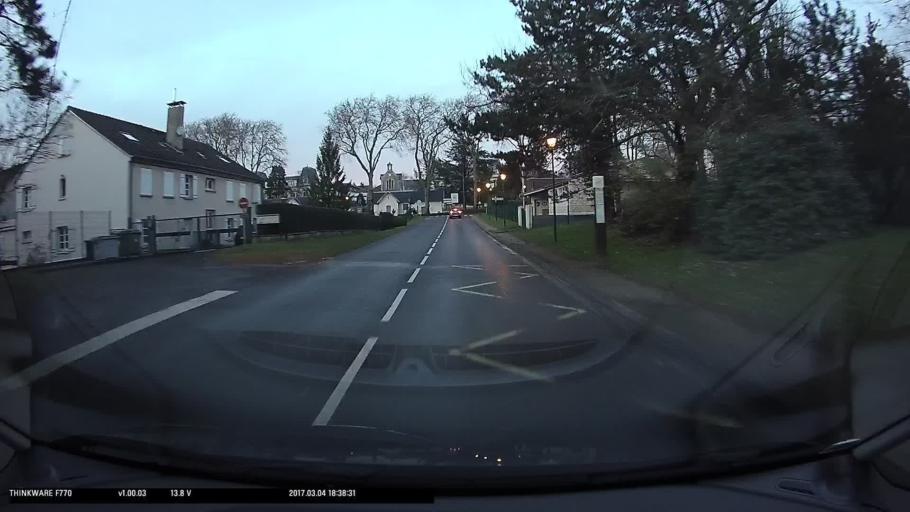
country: FR
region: Ile-de-France
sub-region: Departement du Val-d'Oise
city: Marines
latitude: 49.1457
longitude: 1.9747
